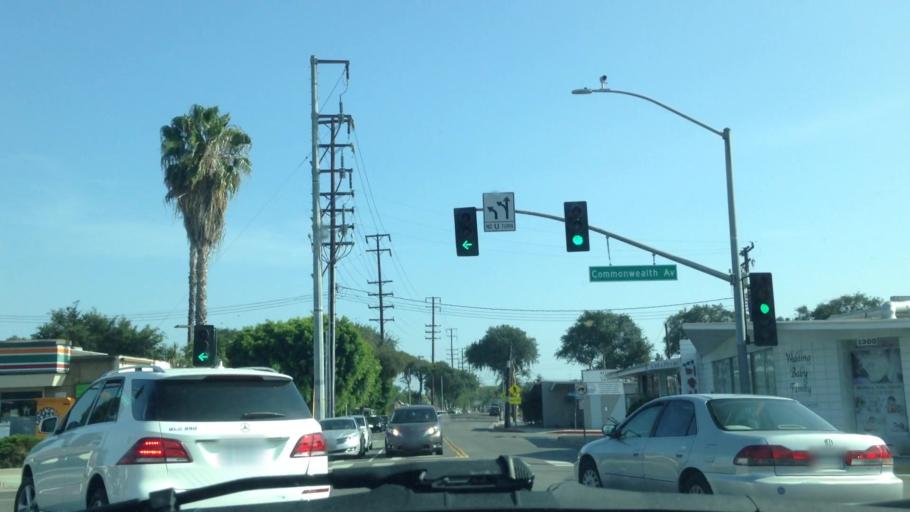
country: US
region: California
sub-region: Orange County
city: Buena Park
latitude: 33.8701
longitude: -117.9683
